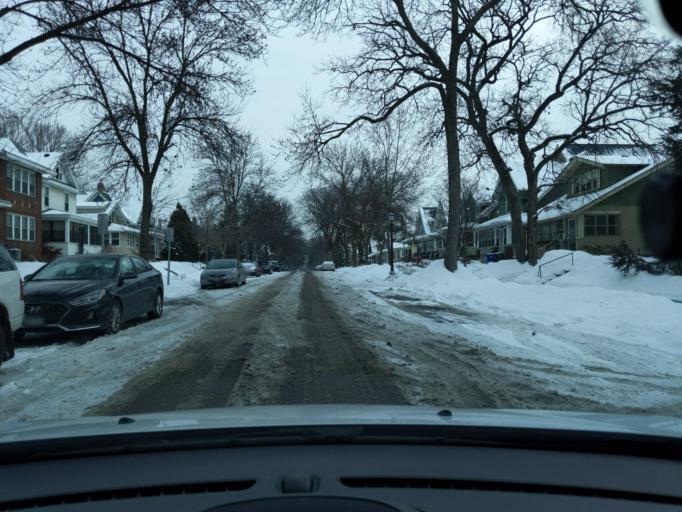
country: US
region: Minnesota
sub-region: Ramsey County
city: Falcon Heights
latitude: 44.9475
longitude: -93.1564
